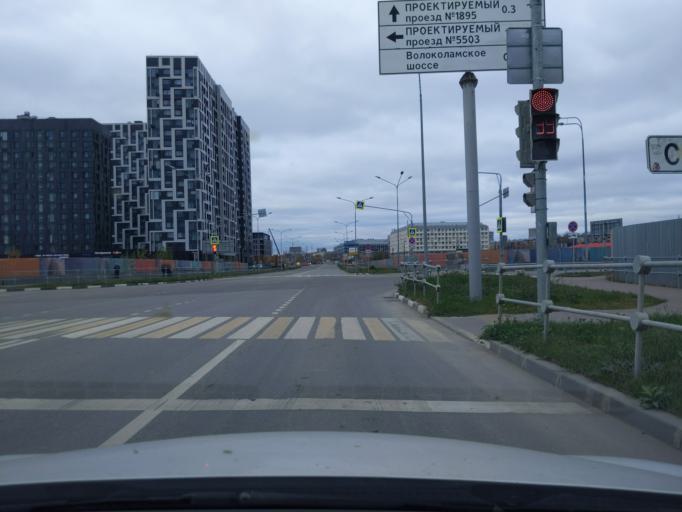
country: RU
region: Moscow
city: Strogino
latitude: 55.8219
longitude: 37.4358
